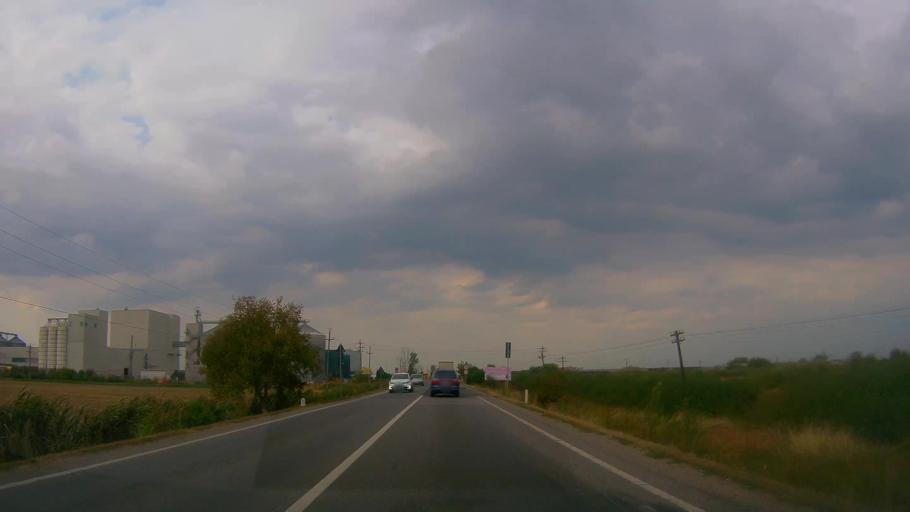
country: RO
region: Satu Mare
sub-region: Comuna Botiz
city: Botiz
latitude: 47.8223
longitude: 22.9406
